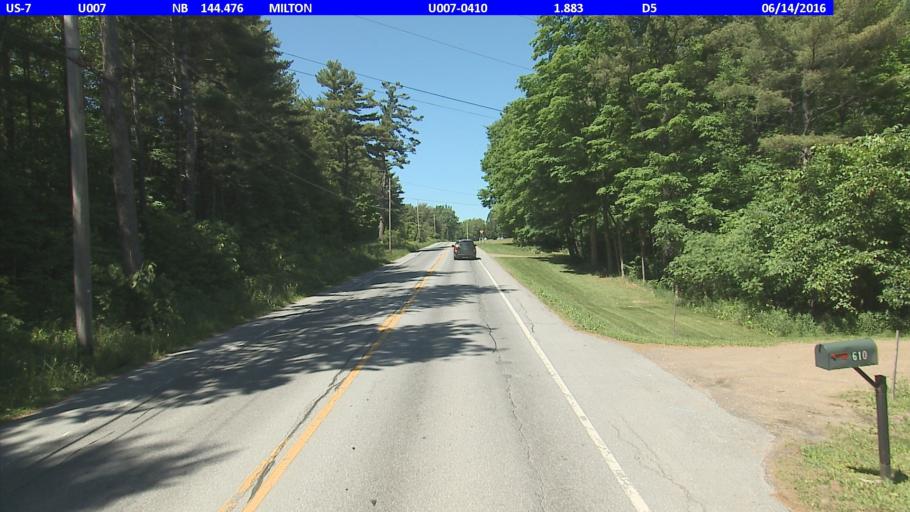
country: US
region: Vermont
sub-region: Chittenden County
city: Milton
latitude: 44.6201
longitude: -73.1489
